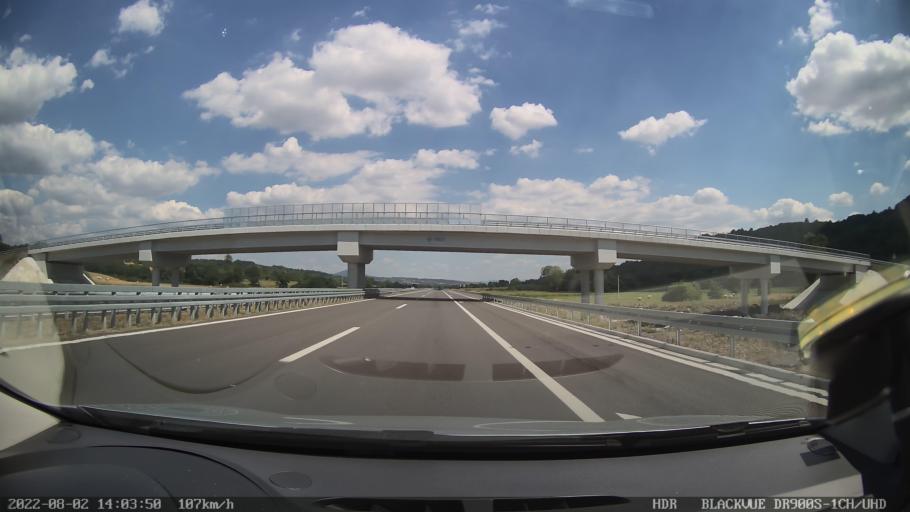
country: RS
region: Central Serbia
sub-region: Moravicki Okrug
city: Cacak
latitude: 43.9243
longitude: 20.3581
